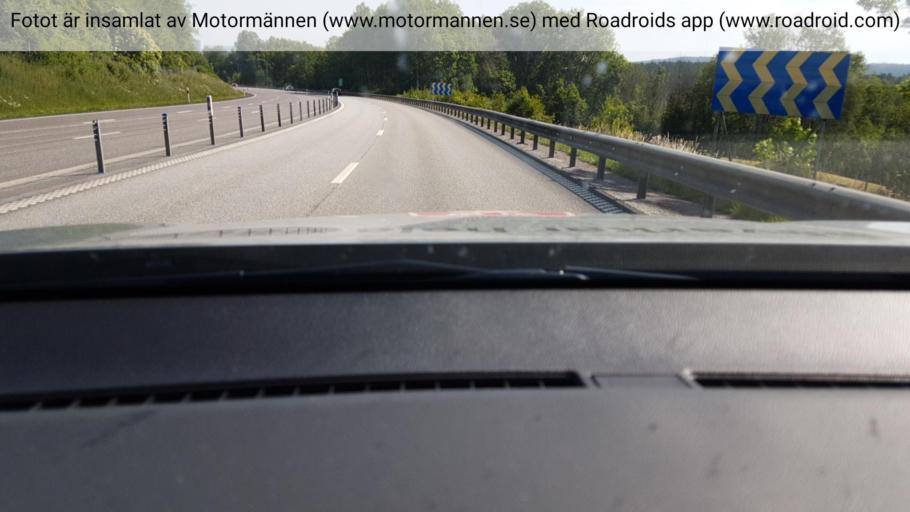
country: SE
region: Joenkoeping
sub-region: Jonkopings Kommun
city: Jonkoping
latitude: 57.7474
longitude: 14.1291
